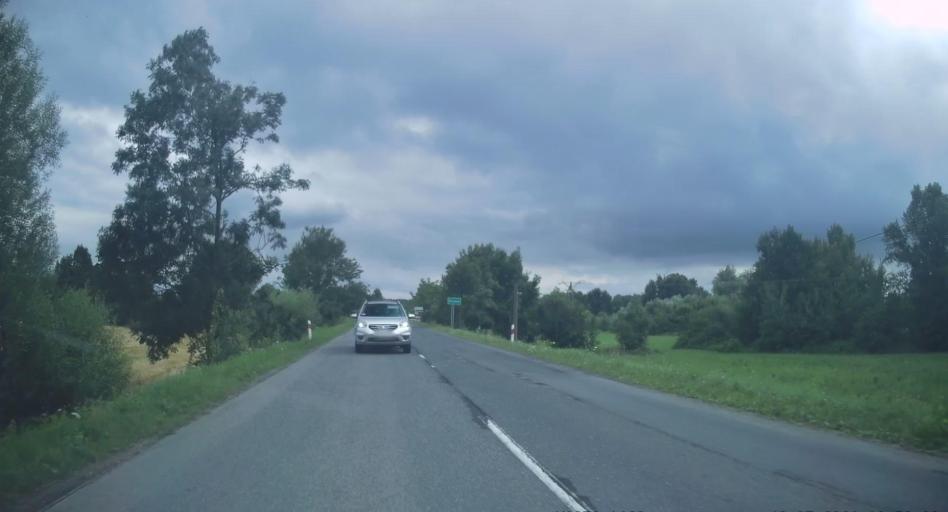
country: PL
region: Opole Voivodeship
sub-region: Powiat nyski
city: Paczkow
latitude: 50.4724
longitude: 17.0113
